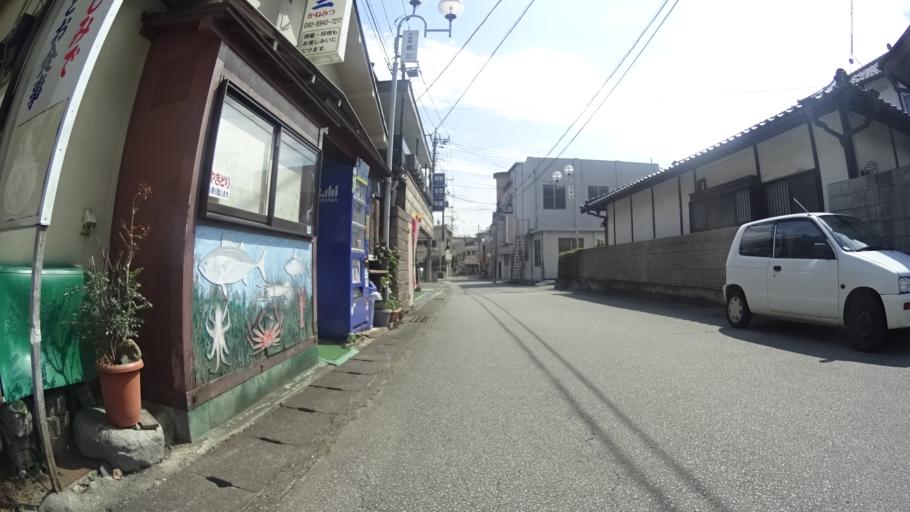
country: JP
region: Yamanashi
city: Enzan
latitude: 35.7073
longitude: 138.7313
